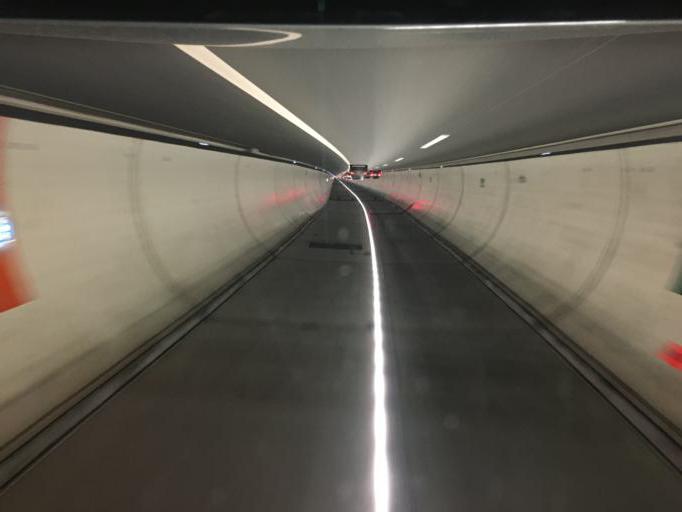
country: CH
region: Zurich
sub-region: Bezirk Affoltern
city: Wettswil / Wettswil (Dorf)
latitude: 47.3446
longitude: 8.4761
